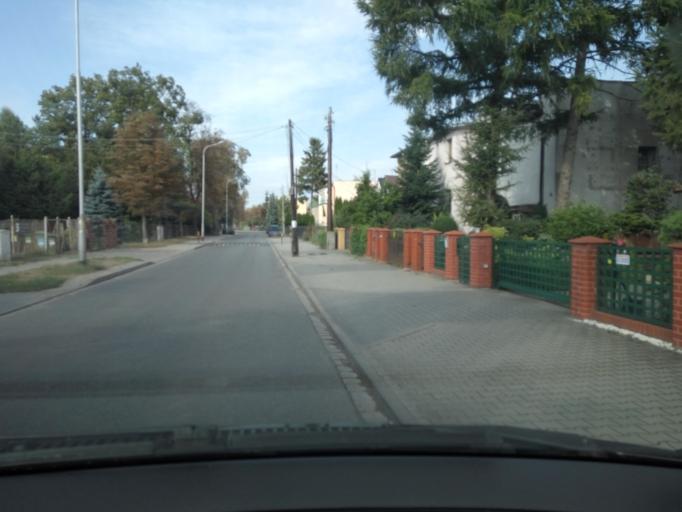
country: PL
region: Lower Silesian Voivodeship
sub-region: Powiat wroclawski
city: Radwanice
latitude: 51.0506
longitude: 17.0833
